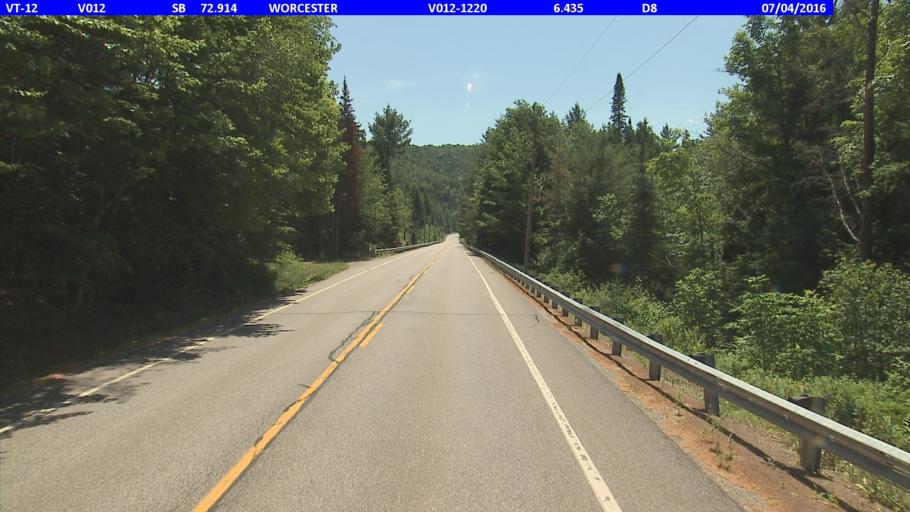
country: US
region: Vermont
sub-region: Lamoille County
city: Morrisville
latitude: 44.4341
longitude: -72.5354
